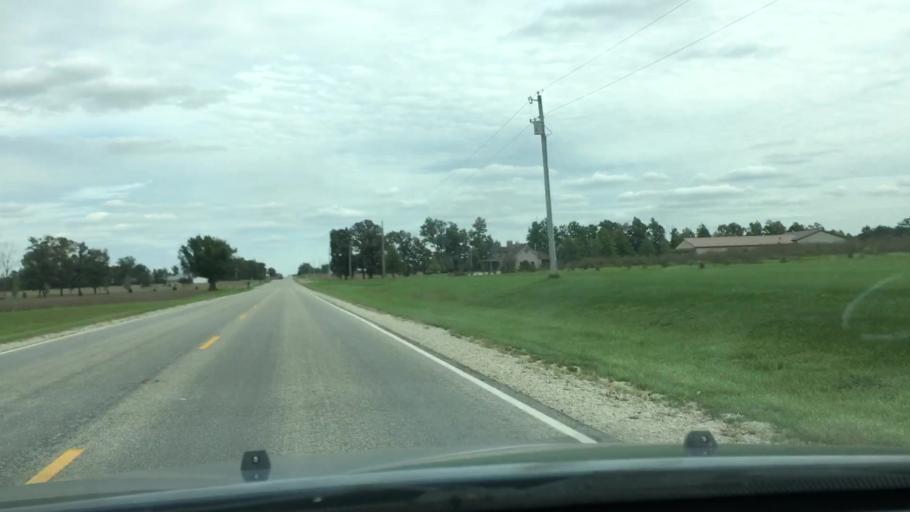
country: US
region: Indiana
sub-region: Adams County
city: Geneva
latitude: 40.5418
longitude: -84.9139
